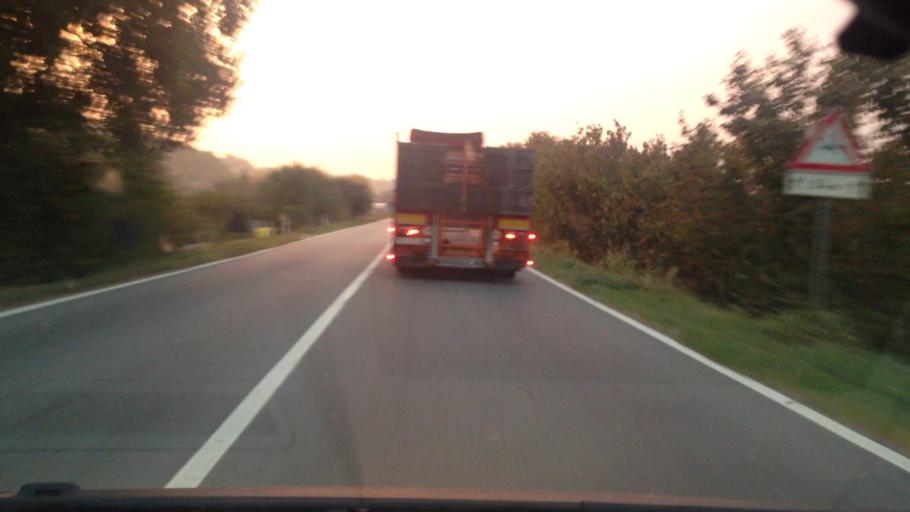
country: IT
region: Piedmont
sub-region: Provincia di Asti
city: Rocca d'Arazzo
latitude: 44.9053
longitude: 8.2861
